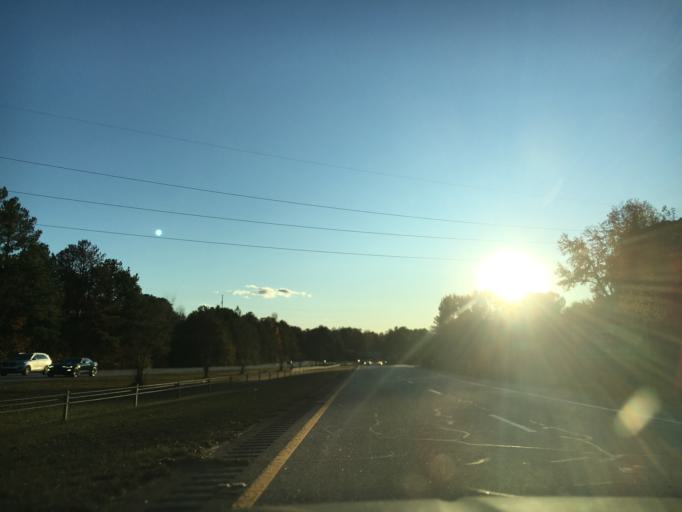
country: US
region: South Carolina
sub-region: Richland County
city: Forest Acres
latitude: 34.0386
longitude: -81.0196
